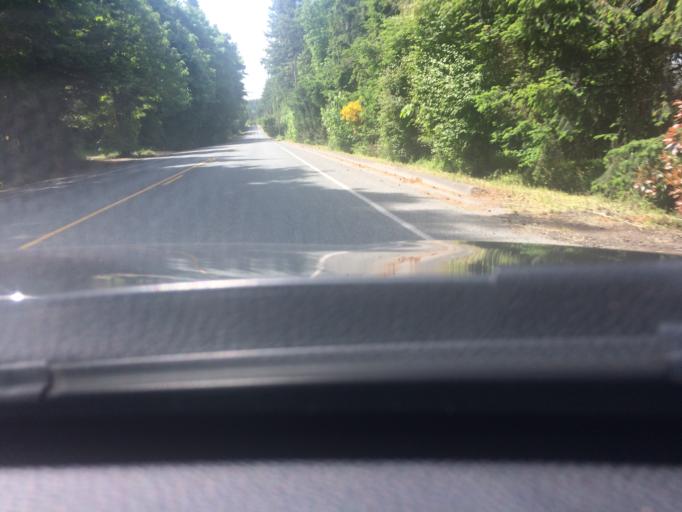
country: US
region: Washington
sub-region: Skagit County
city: Anacortes
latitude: 48.4488
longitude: -122.6572
